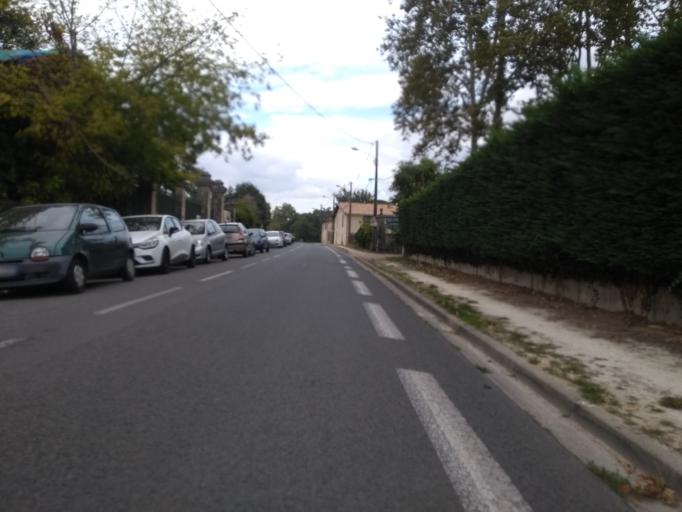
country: FR
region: Aquitaine
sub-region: Departement de la Gironde
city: Pessac
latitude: 44.8242
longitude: -0.6489
